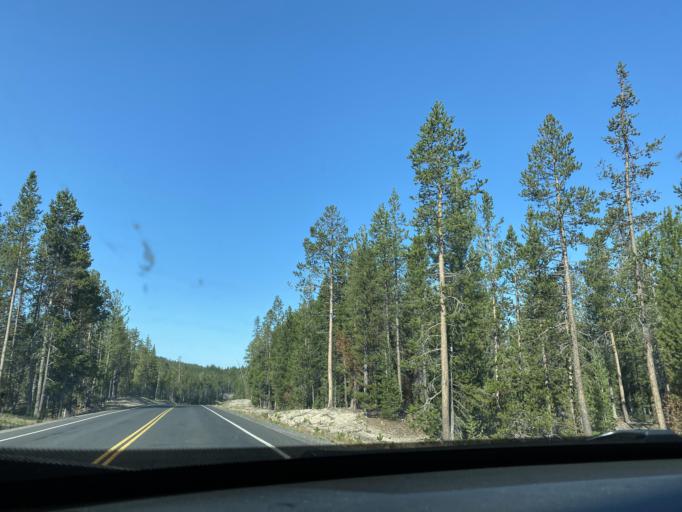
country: US
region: Oregon
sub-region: Deschutes County
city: Three Rivers
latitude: 43.7055
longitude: -121.2458
